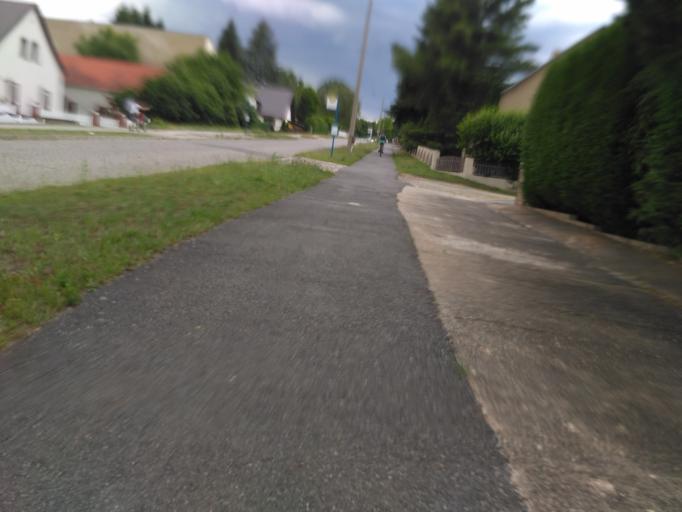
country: DE
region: Brandenburg
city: Elsterwerda
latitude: 51.4728
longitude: 13.5124
